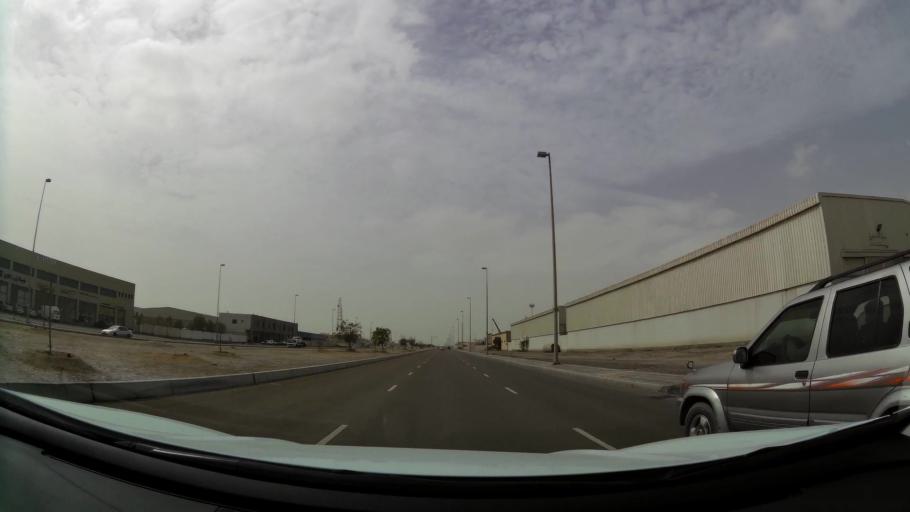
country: AE
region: Abu Dhabi
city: Abu Dhabi
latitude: 24.3681
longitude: 54.4896
